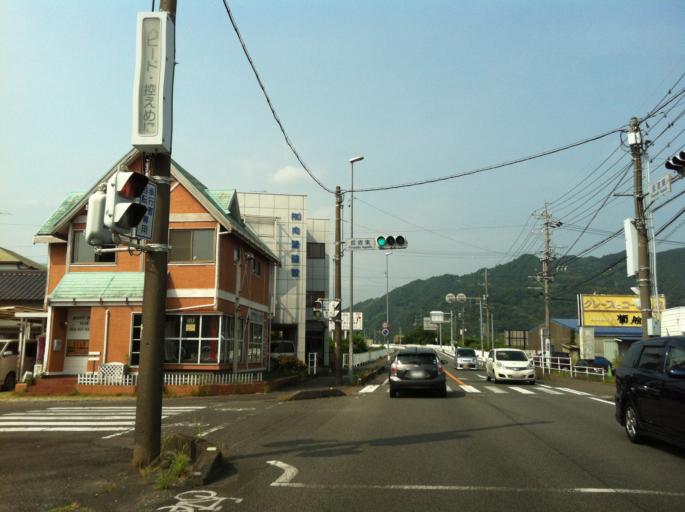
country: JP
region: Shizuoka
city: Fujieda
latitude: 34.8956
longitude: 138.2833
